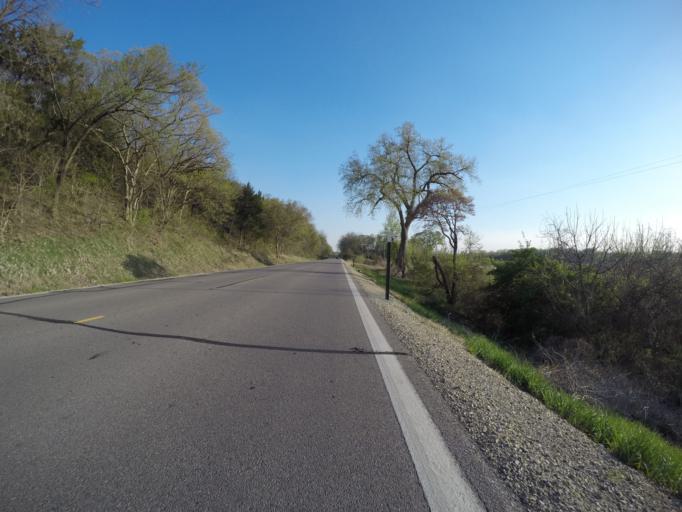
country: US
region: Kansas
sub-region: Riley County
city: Manhattan
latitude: 39.1564
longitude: -96.5571
